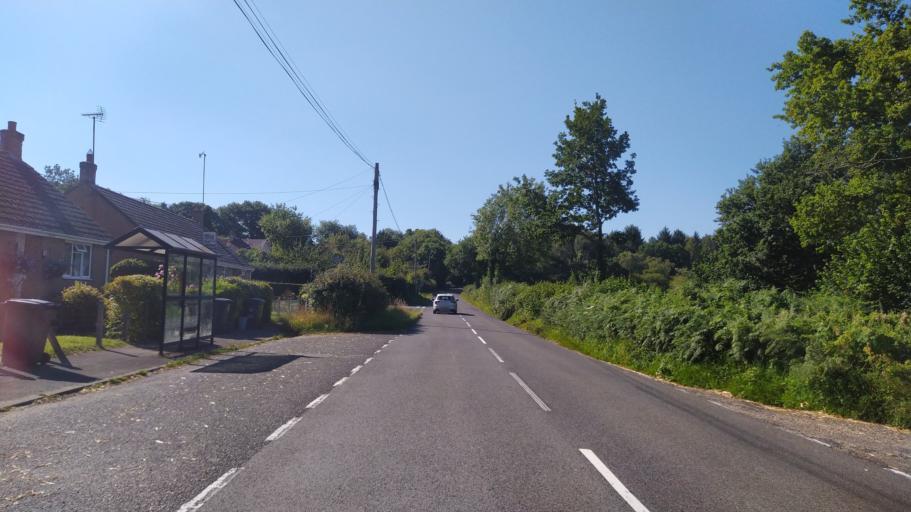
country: GB
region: England
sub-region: Dorset
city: Lytchett Matravers
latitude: 50.7512
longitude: -2.1237
